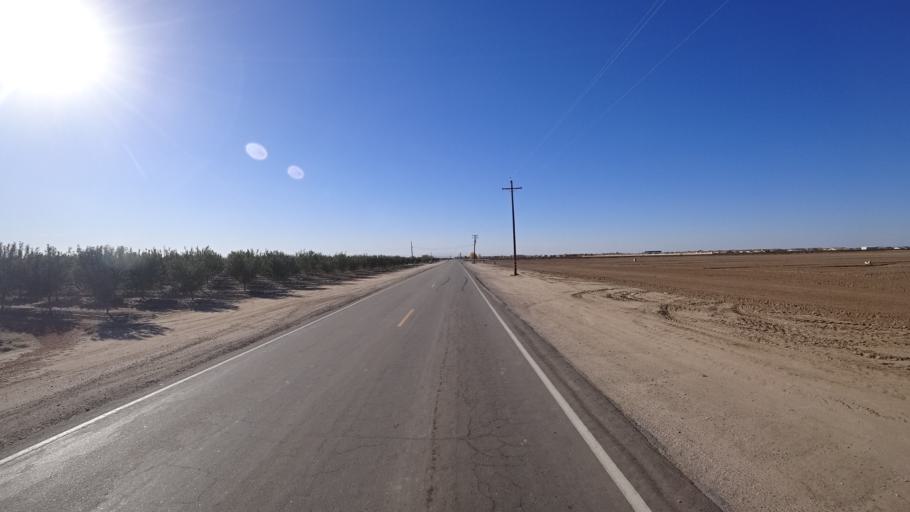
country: US
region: California
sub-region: Kern County
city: Greenfield
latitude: 35.2817
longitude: -119.0971
